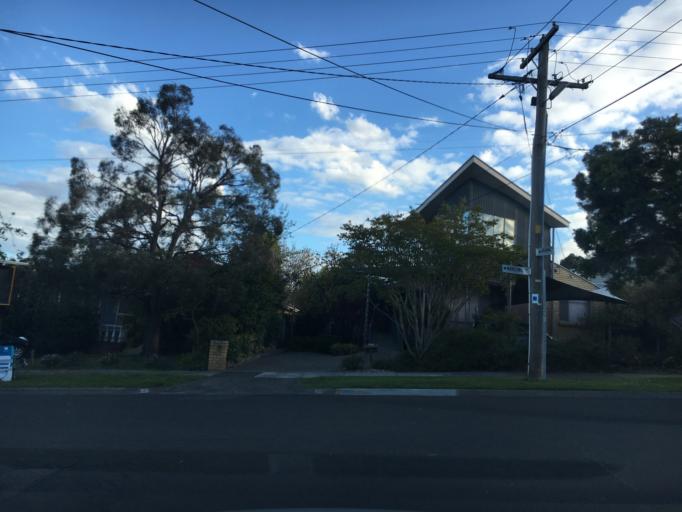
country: AU
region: Victoria
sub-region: Whitehorse
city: Vermont South
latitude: -37.8774
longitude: 145.1731
